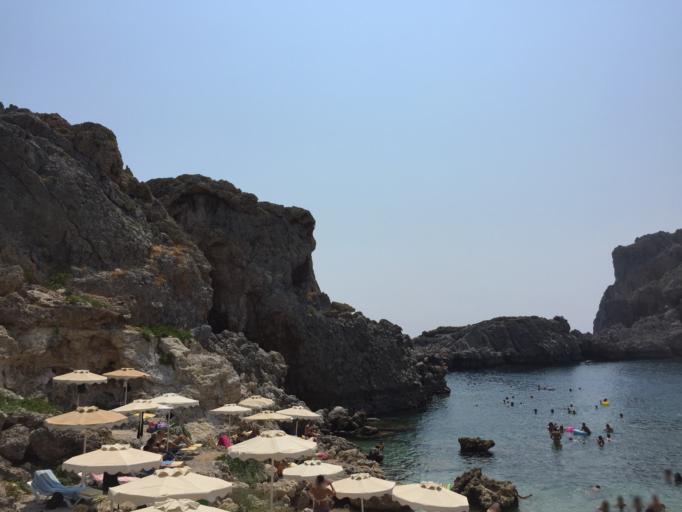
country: GR
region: South Aegean
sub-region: Nomos Dodekanisou
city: Lardos
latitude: 36.0883
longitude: 28.0879
